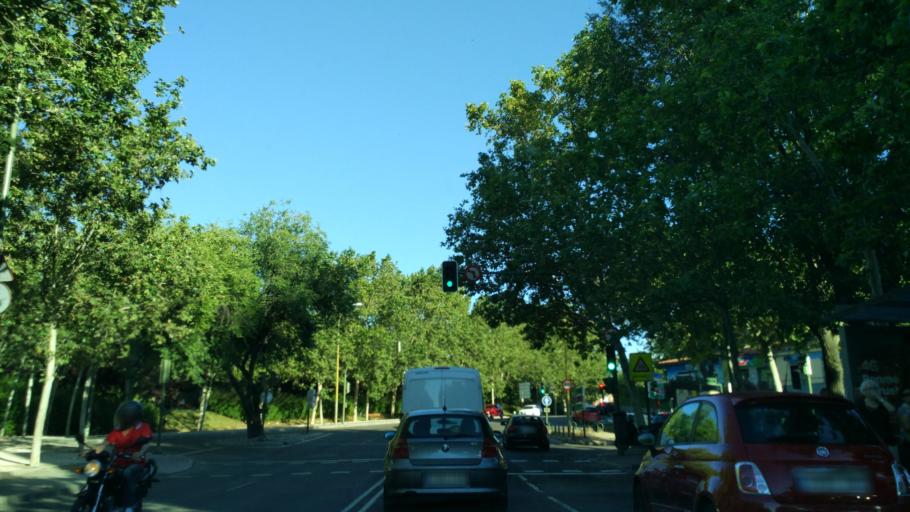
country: ES
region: Madrid
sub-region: Provincia de Madrid
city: Tetuan de las Victorias
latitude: 40.4647
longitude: -3.7097
